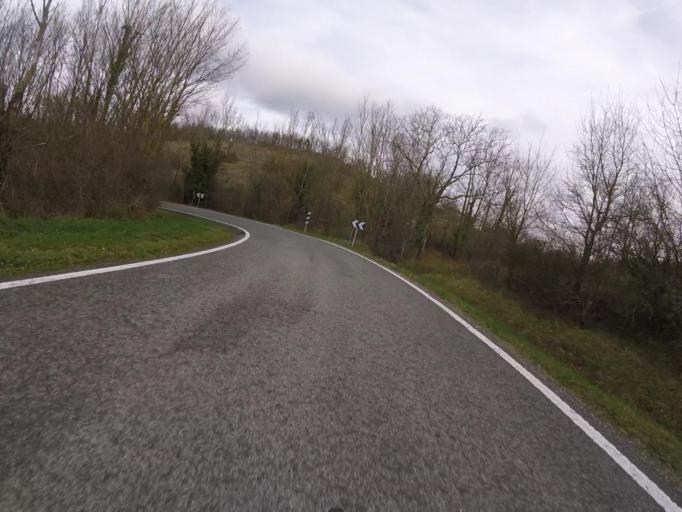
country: ES
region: Navarre
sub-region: Provincia de Navarra
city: Olazagutia
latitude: 42.8806
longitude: -2.1782
